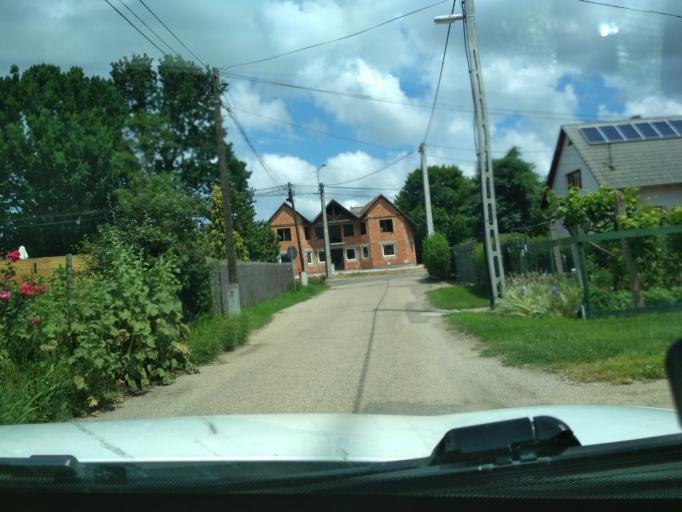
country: HU
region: Jasz-Nagykun-Szolnok
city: Tiszafured
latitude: 47.6182
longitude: 20.7428
